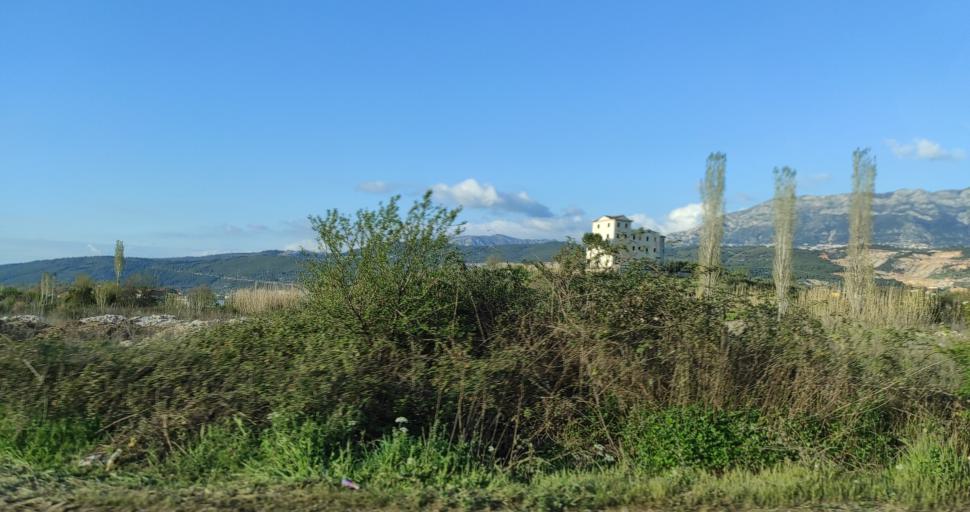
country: AL
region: Durres
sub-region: Rrethi i Krujes
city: Fushe-Kruje
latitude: 41.4850
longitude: 19.7309
